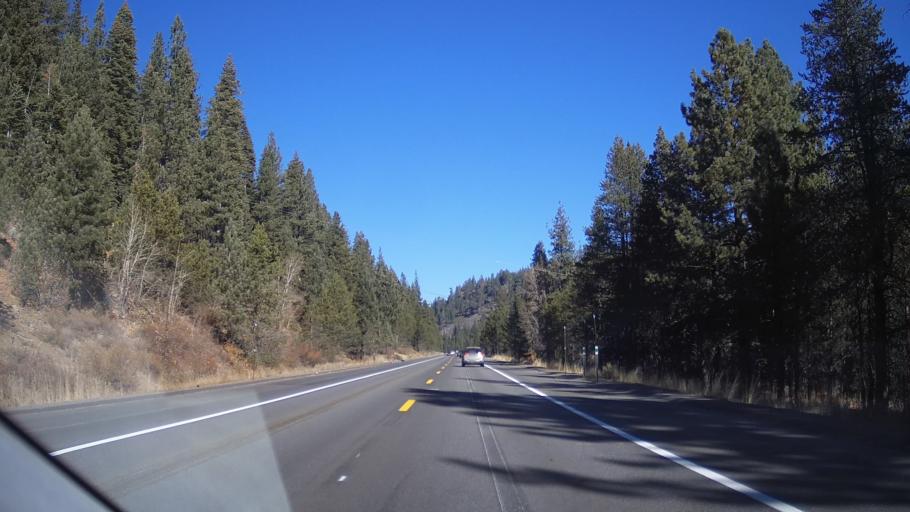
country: US
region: California
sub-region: Nevada County
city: Truckee
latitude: 39.2930
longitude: -120.2075
